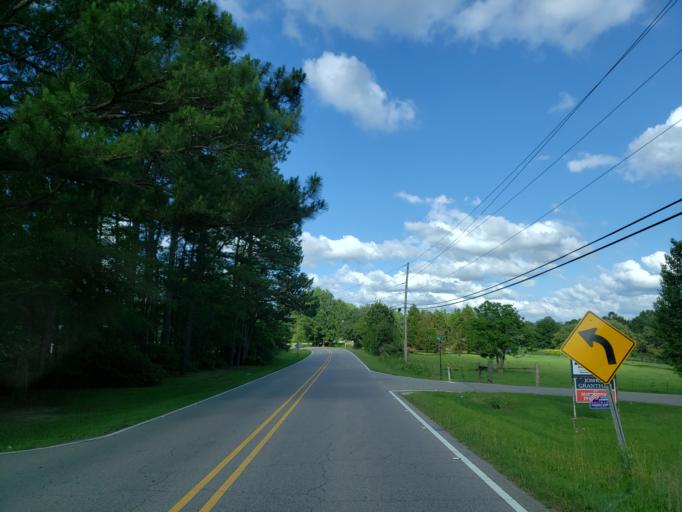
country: US
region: Mississippi
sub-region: Lamar County
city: West Hattiesburg
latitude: 31.2805
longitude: -89.4319
